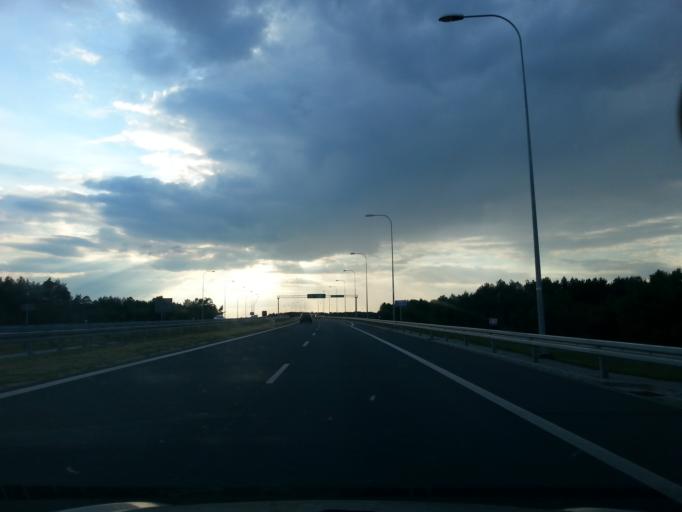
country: PL
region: Lodz Voivodeship
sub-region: Powiat zdunskowolski
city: Zapolice
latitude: 51.5954
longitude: 18.8820
